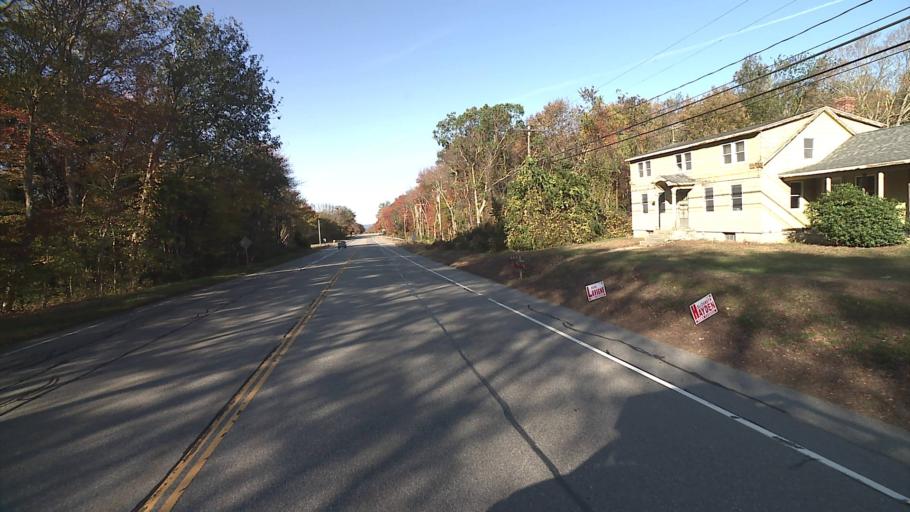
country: US
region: Connecticut
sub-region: Windham County
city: Danielson
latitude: 41.7908
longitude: -71.8149
